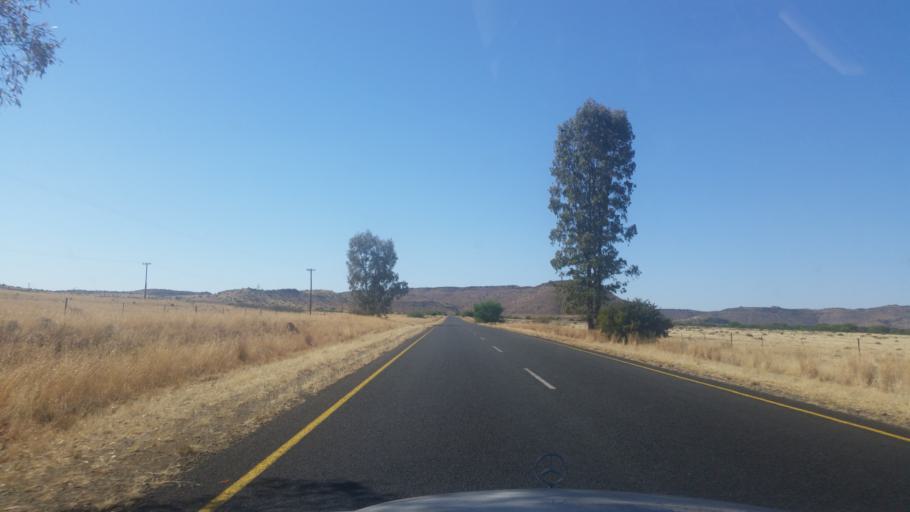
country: ZA
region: Orange Free State
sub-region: Xhariep District Municipality
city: Trompsburg
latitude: -30.5005
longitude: 26.0084
